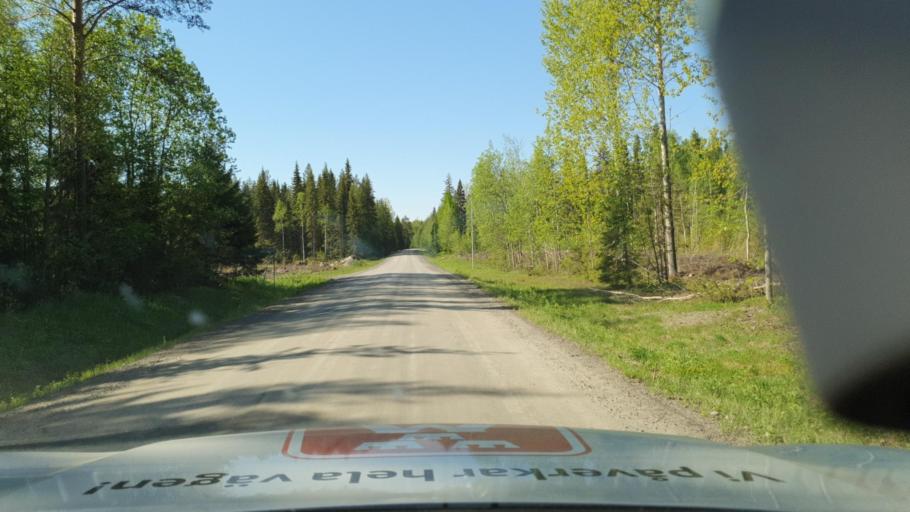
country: SE
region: Vaesterbotten
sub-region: Vannas Kommun
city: Vaennaes
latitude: 64.0202
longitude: 19.7511
